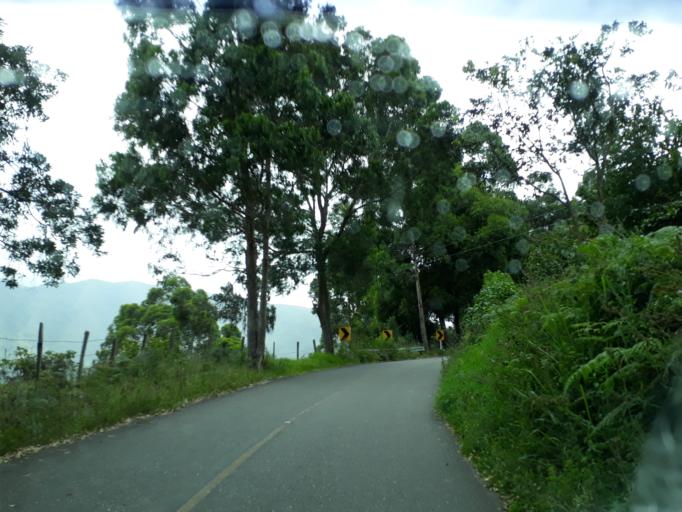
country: CO
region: Cundinamarca
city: Cabrera
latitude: 4.0170
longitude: -74.5110
